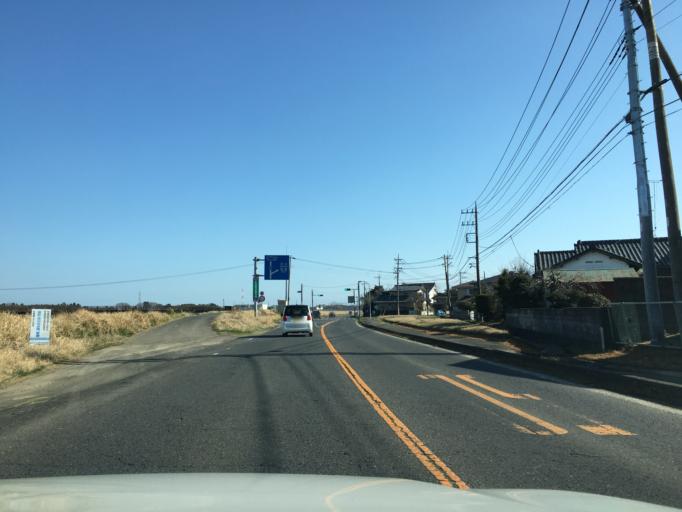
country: JP
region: Ibaraki
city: Mito-shi
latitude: 36.4379
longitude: 140.4166
